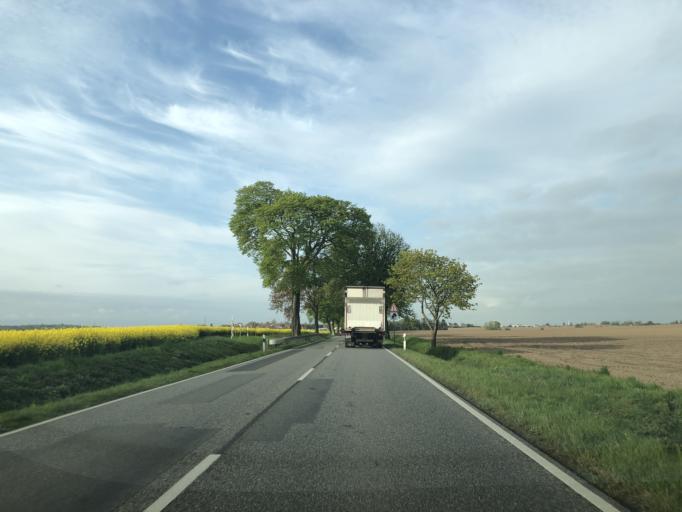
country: DE
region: Mecklenburg-Vorpommern
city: Guestrow
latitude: 53.8519
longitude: 12.2259
